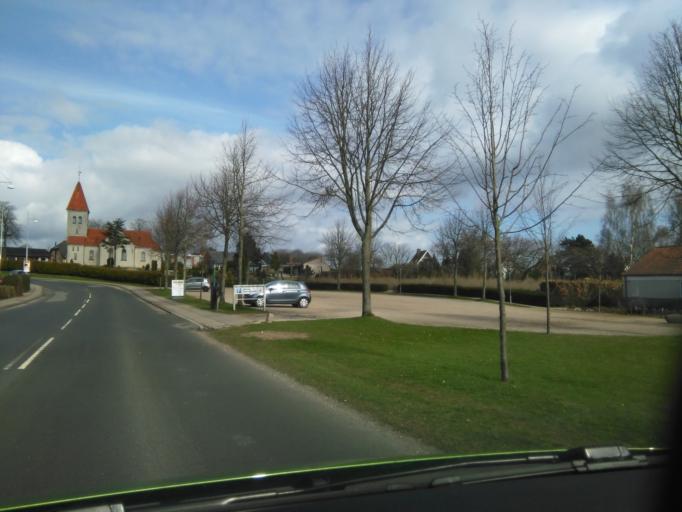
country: DK
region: South Denmark
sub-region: Middelfart Kommune
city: Strib
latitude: 55.5365
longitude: 9.7730
